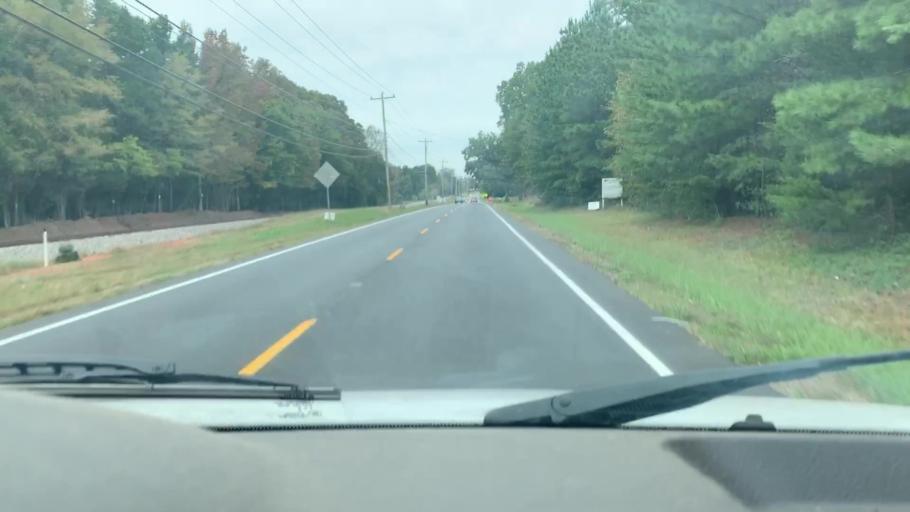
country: US
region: North Carolina
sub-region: Gaston County
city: Davidson
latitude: 35.5296
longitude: -80.8448
